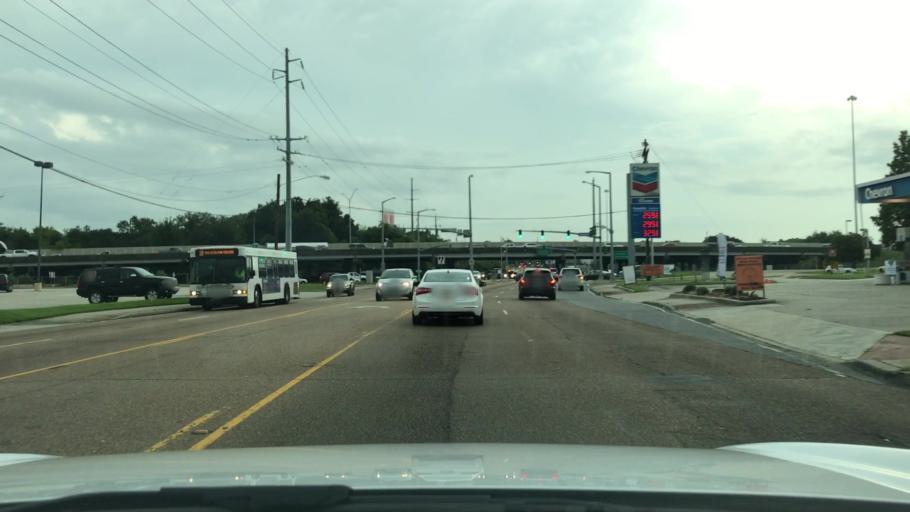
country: US
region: Louisiana
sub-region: East Baton Rouge Parish
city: Baton Rouge
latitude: 30.4215
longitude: -91.1403
